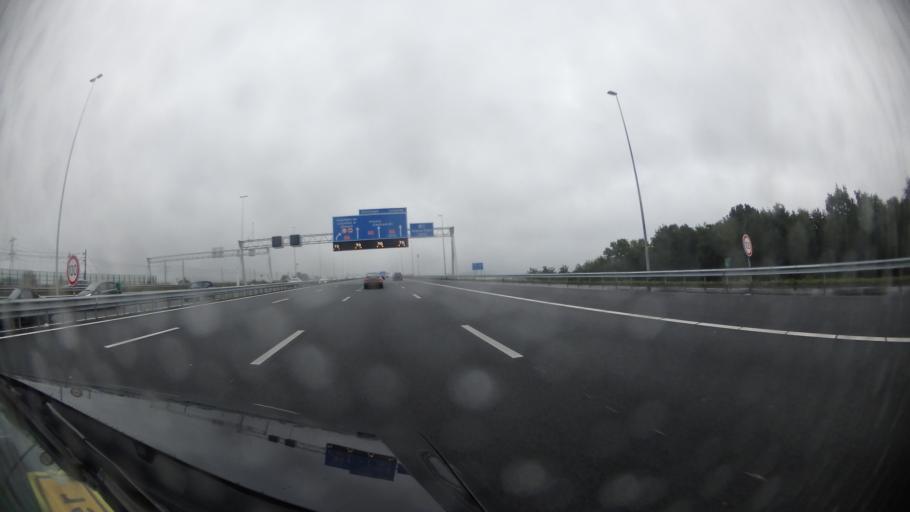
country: NL
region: North Holland
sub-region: Gemeente Naarden
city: Naarden
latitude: 52.3235
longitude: 5.1357
